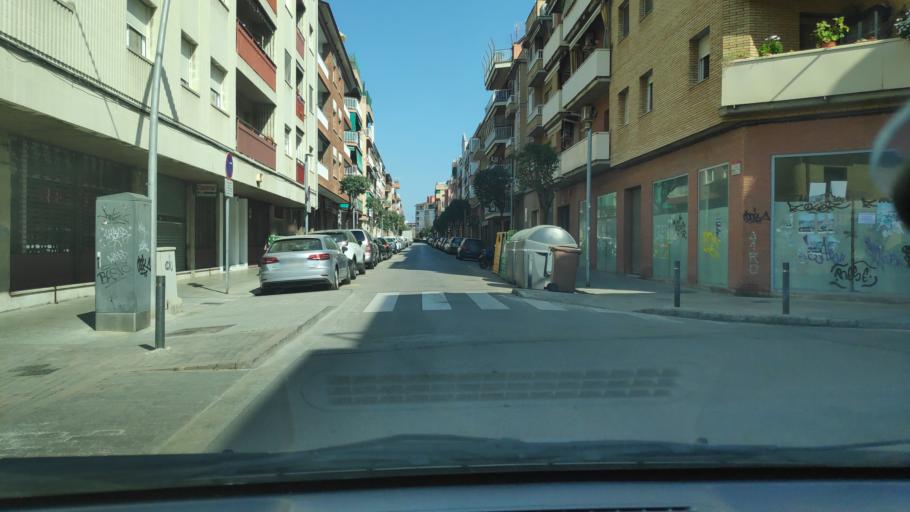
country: ES
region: Catalonia
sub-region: Provincia de Barcelona
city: Mollet del Valles
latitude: 41.5398
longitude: 2.2162
